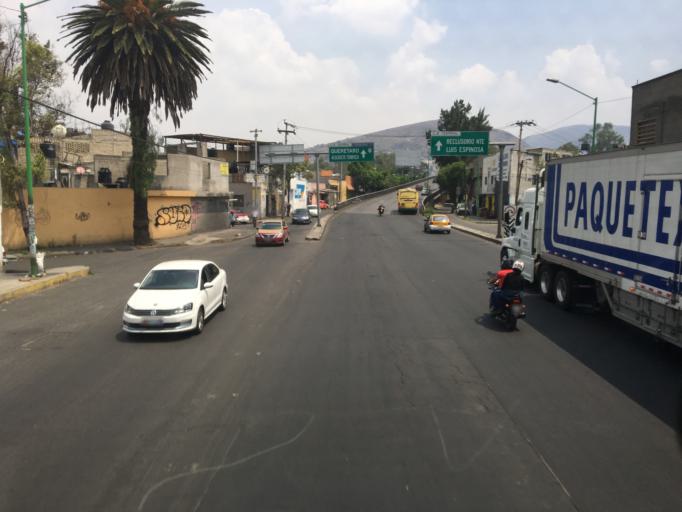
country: MX
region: Mexico
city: Tlalnepantla
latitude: 19.5236
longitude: -99.1583
